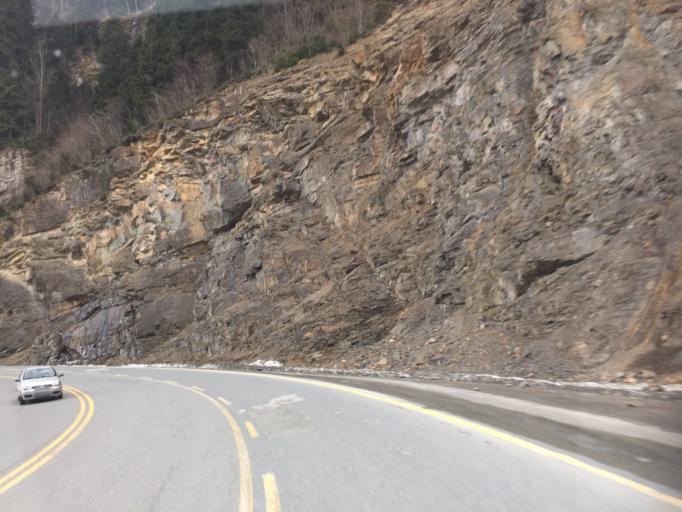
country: TR
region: Gumushane
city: Yaglidere
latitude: 40.6998
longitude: 39.4659
